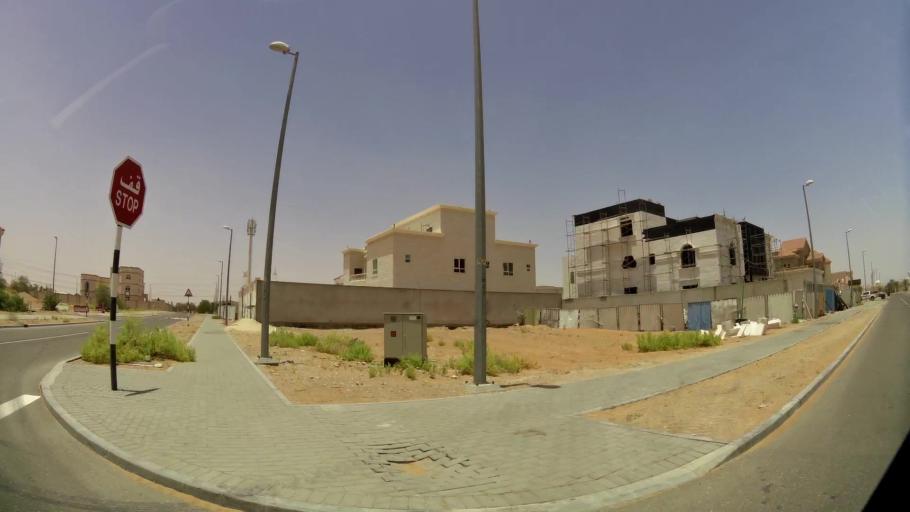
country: OM
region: Al Buraimi
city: Al Buraymi
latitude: 24.2690
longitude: 55.7099
